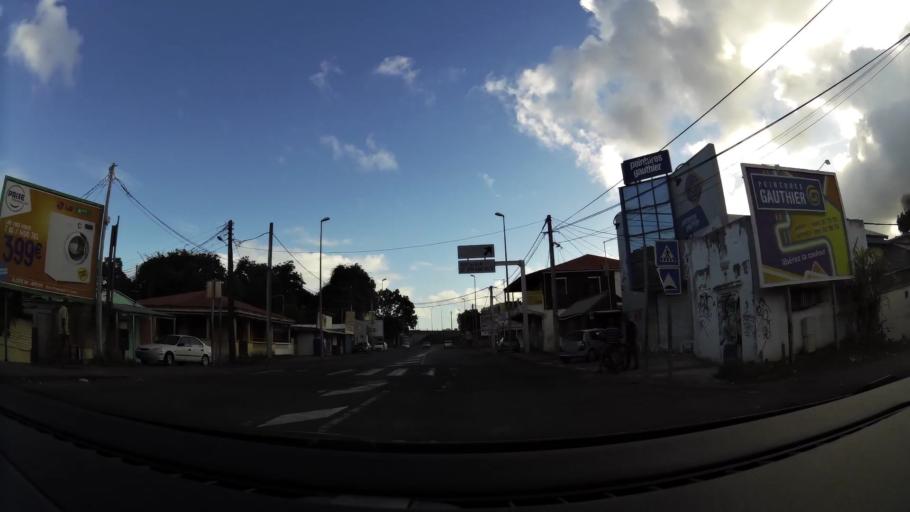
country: GP
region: Guadeloupe
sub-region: Guadeloupe
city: Pointe-a-Pitre
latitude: 16.2492
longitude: -61.5305
